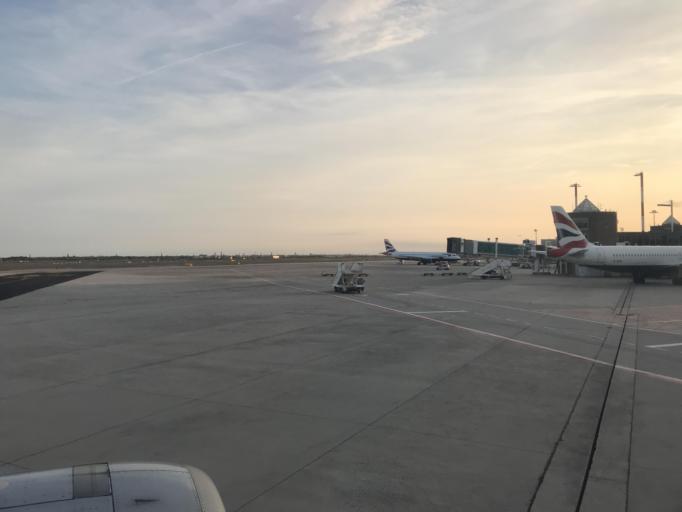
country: IT
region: Veneto
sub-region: Provincia di Venezia
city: Tessera
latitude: 45.5053
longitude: 12.3433
